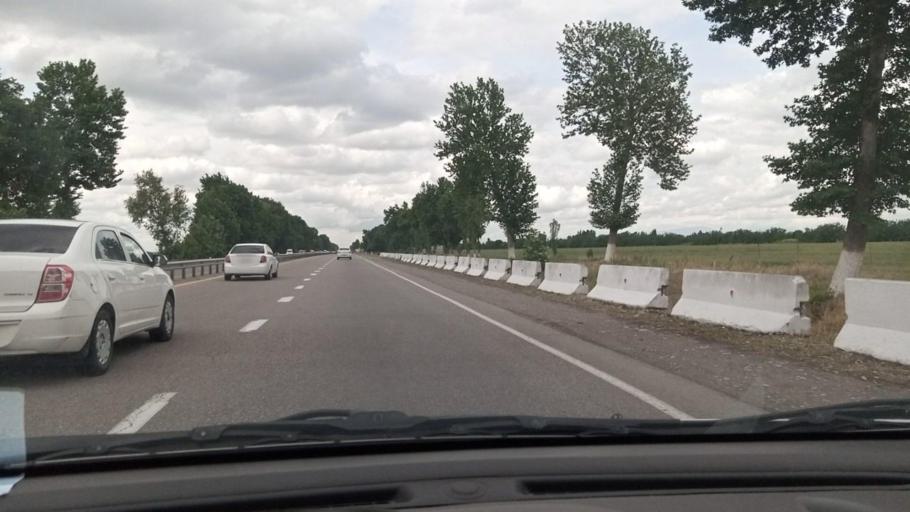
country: UZ
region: Toshkent Shahri
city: Bektemir
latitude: 41.2002
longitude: 69.4031
